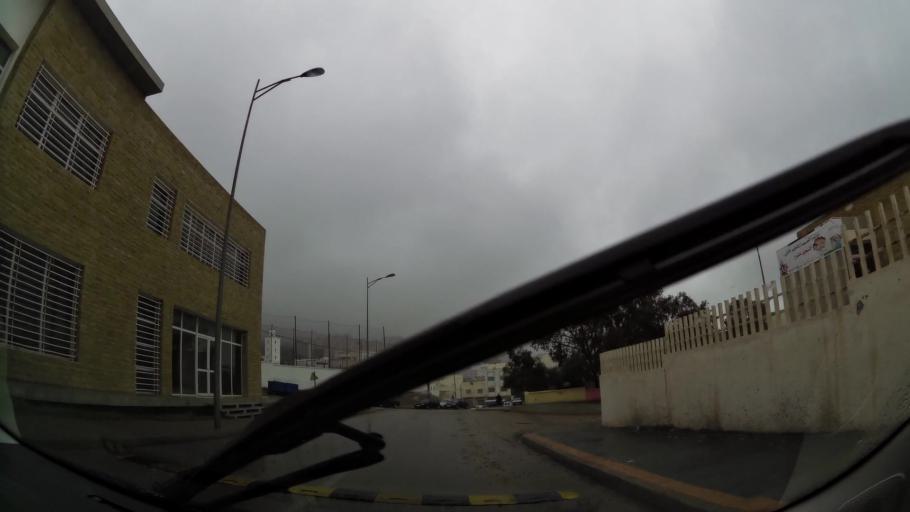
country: MA
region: Taza-Al Hoceima-Taounate
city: Al Hoceima
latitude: 35.2493
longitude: -3.9466
